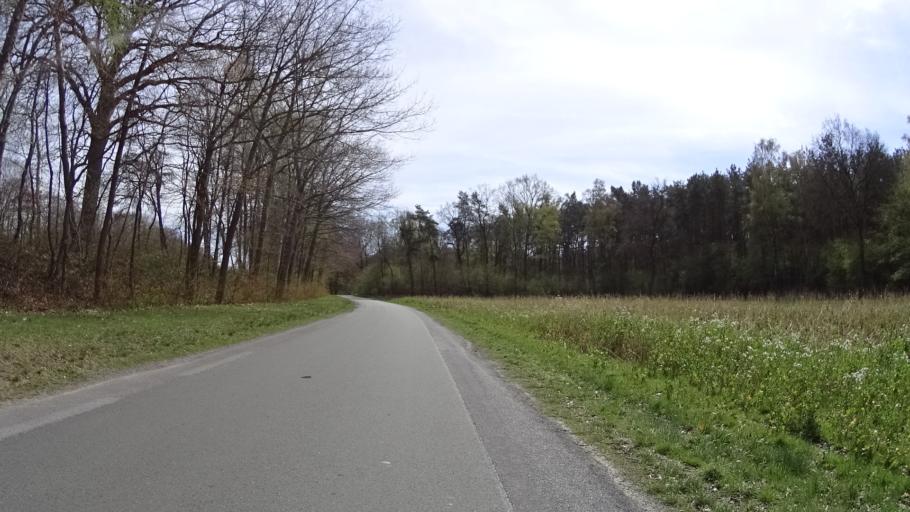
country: DE
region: Lower Saxony
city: Emsburen
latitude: 52.4197
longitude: 7.3572
